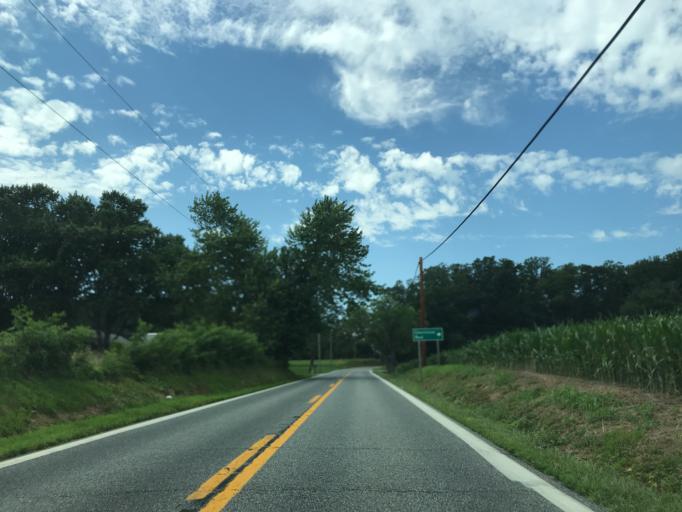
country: US
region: Pennsylvania
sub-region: York County
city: Susquehanna Trails
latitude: 39.7025
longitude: -76.4230
